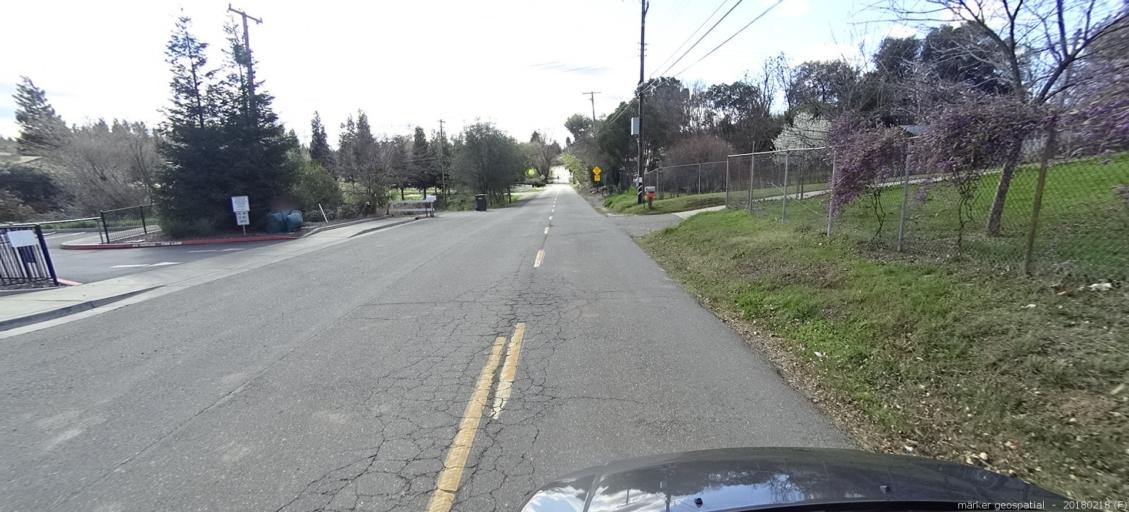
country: US
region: California
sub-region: Sacramento County
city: Folsom
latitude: 38.6955
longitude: -121.1948
